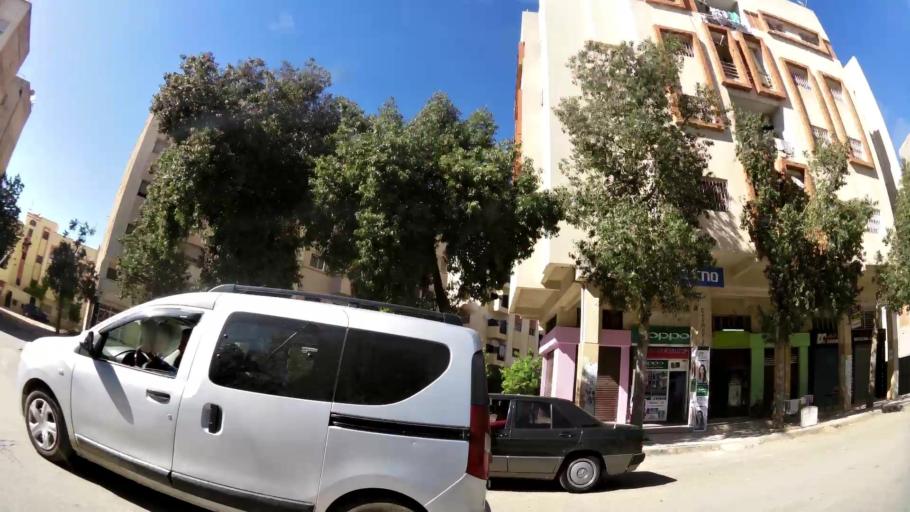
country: MA
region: Fes-Boulemane
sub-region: Fes
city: Fes
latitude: 34.0162
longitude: -4.9752
